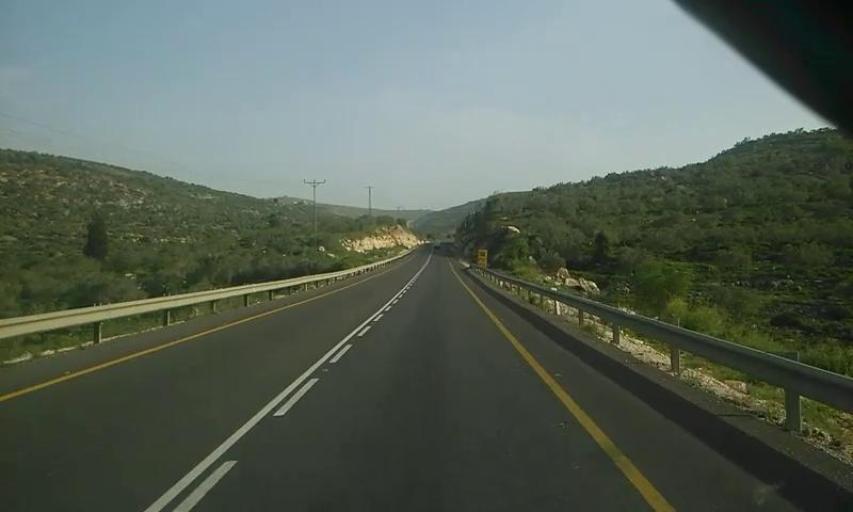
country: PS
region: West Bank
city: Jit
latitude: 32.2228
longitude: 35.1740
